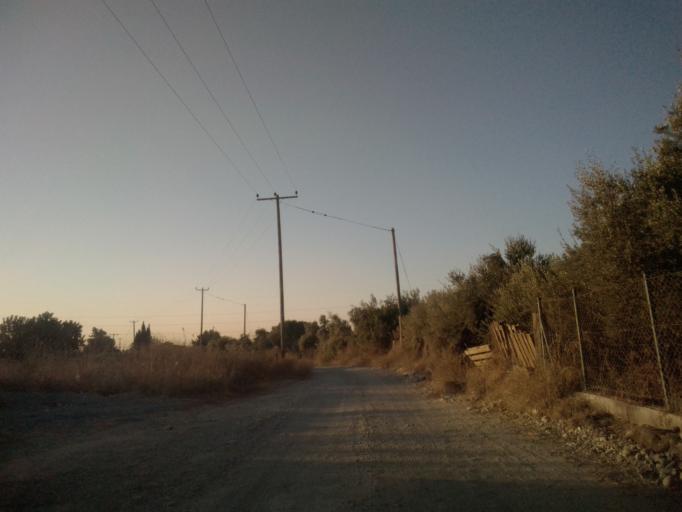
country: CY
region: Limassol
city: Ypsonas
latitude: 34.6692
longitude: 32.9663
